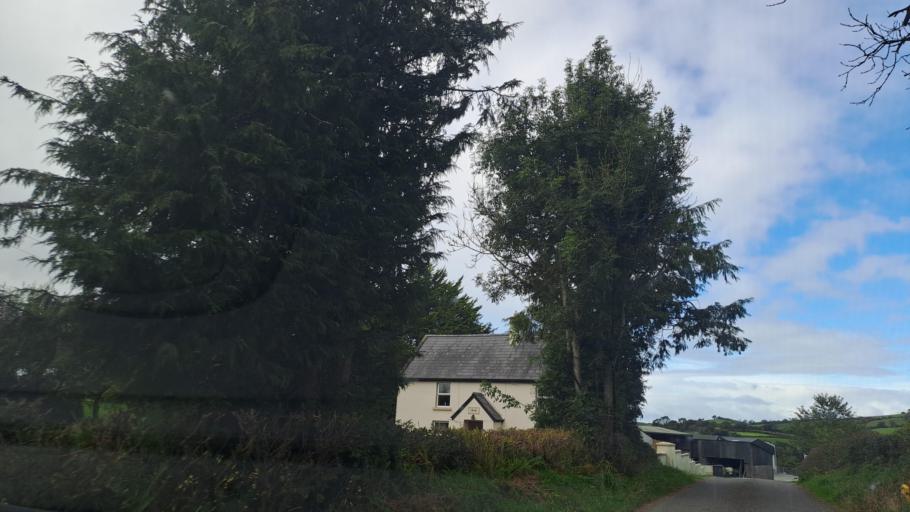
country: IE
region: Ulster
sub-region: An Cabhan
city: Kingscourt
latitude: 53.9958
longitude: -6.8088
